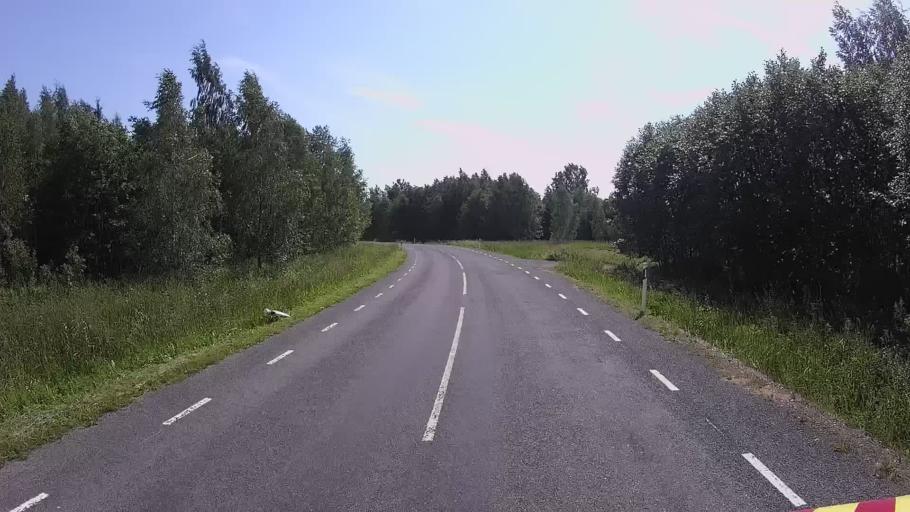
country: EE
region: Viljandimaa
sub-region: Karksi vald
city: Karksi-Nuia
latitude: 58.0454
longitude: 25.5454
